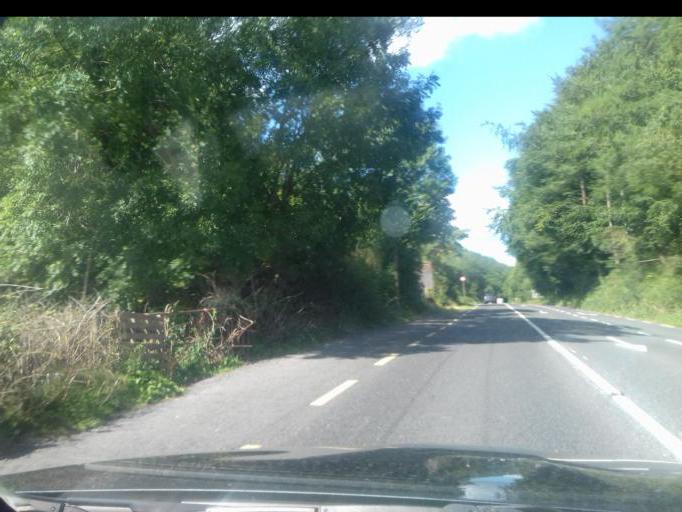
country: IE
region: Munster
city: Carrick-on-Suir
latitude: 52.4072
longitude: -7.4845
